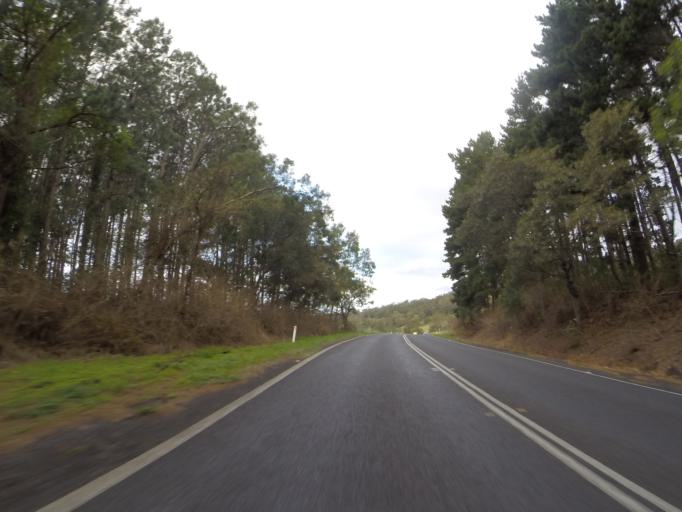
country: AU
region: New South Wales
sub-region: Shellharbour
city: Calderwood
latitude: -34.5811
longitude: 150.7139
